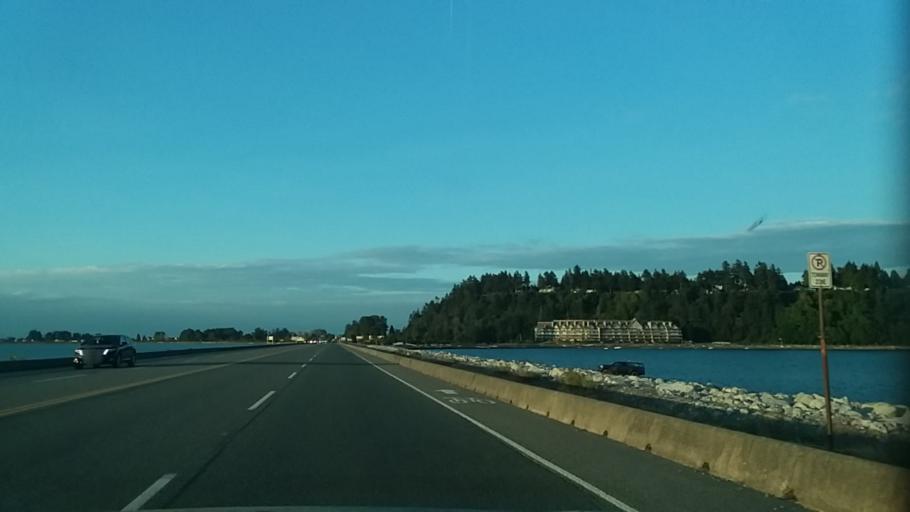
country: US
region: Washington
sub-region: Whatcom County
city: Point Roberts
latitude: 49.0202
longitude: -123.1104
